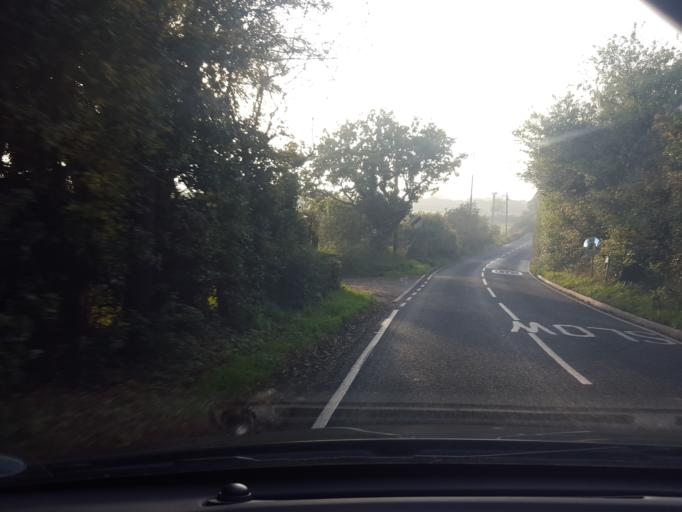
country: GB
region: England
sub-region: Essex
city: Little Clacton
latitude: 51.8237
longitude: 1.1888
